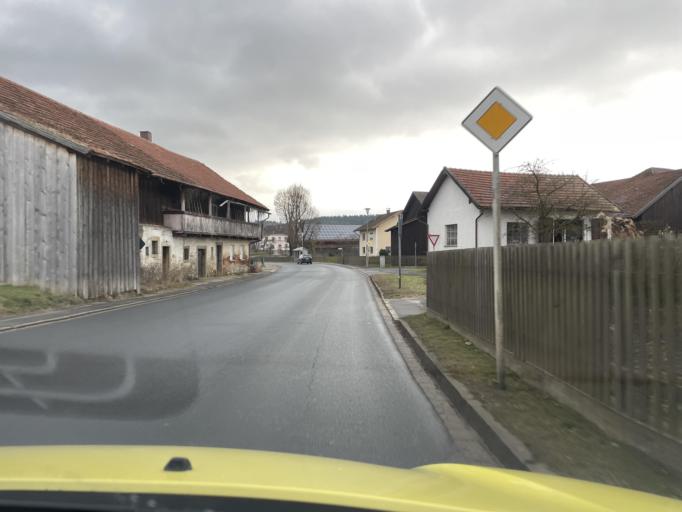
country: DE
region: Bavaria
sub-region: Upper Palatinate
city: Zandt
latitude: 49.1694
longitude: 12.6961
